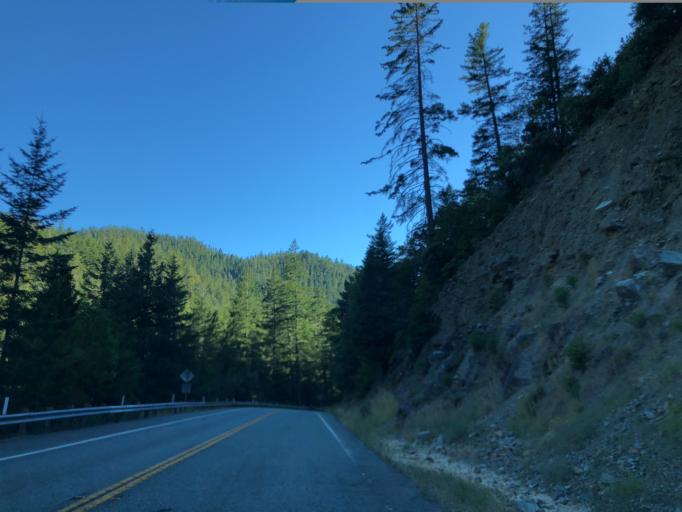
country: US
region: California
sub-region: Del Norte County
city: Bertsch-Oceanview
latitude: 41.8646
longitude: -123.8645
